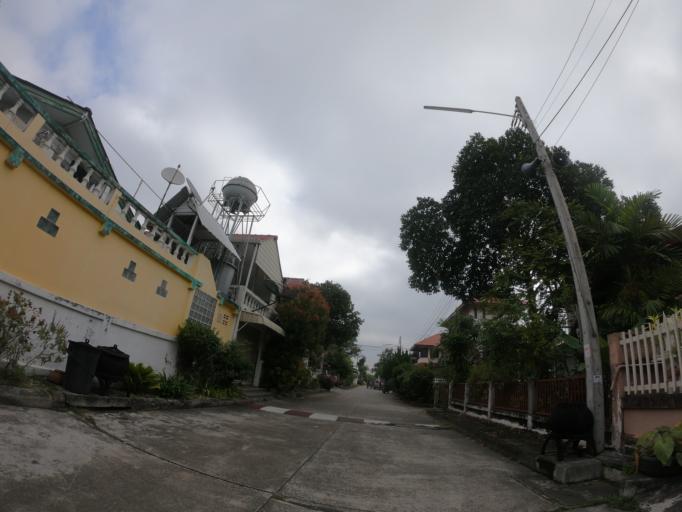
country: TH
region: Chiang Mai
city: Chiang Mai
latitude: 18.7602
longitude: 98.9742
